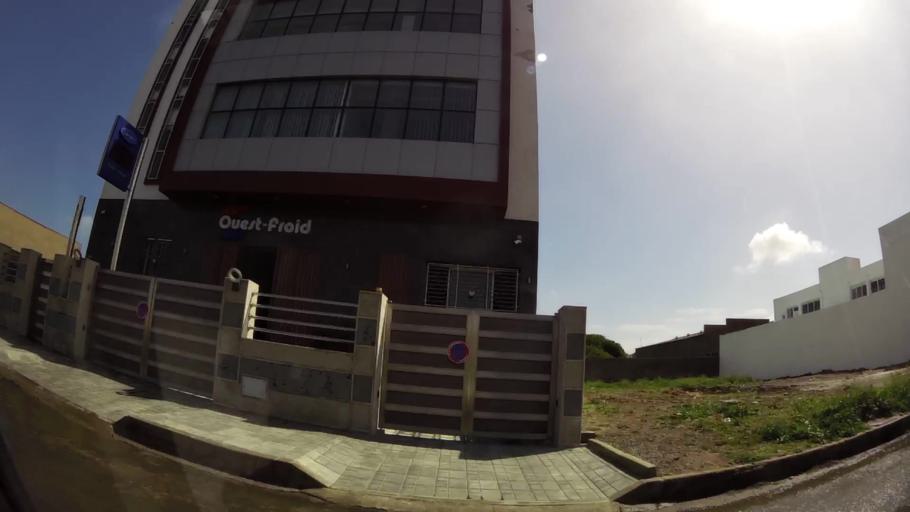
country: MA
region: Grand Casablanca
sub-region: Mediouna
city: Tit Mellil
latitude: 33.6205
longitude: -7.5115
